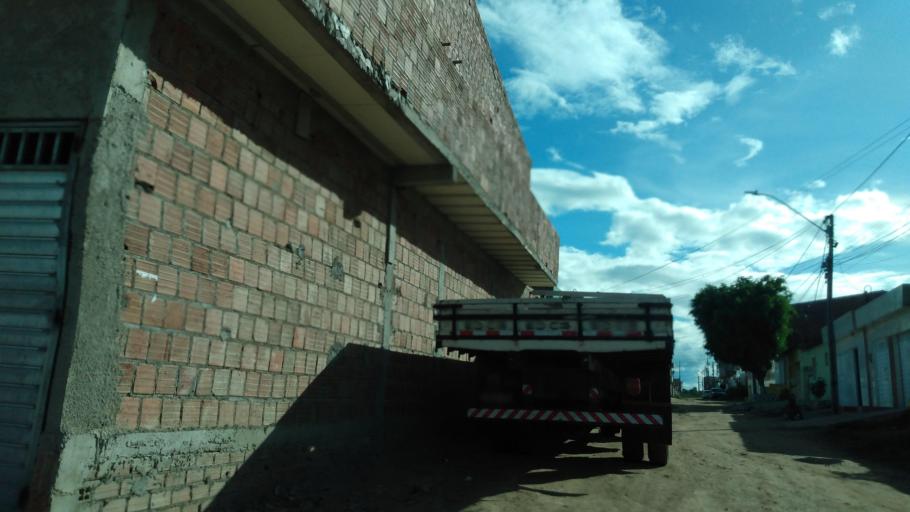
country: BR
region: Pernambuco
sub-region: Gravata
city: Gravata
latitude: -8.2008
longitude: -35.5794
